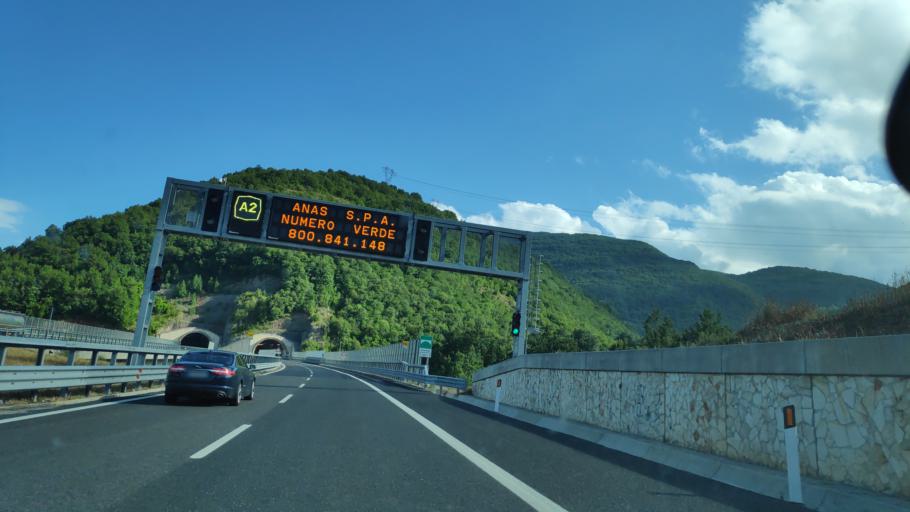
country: IT
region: Campania
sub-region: Provincia di Salerno
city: Casalbuono
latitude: 40.2160
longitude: 15.6720
